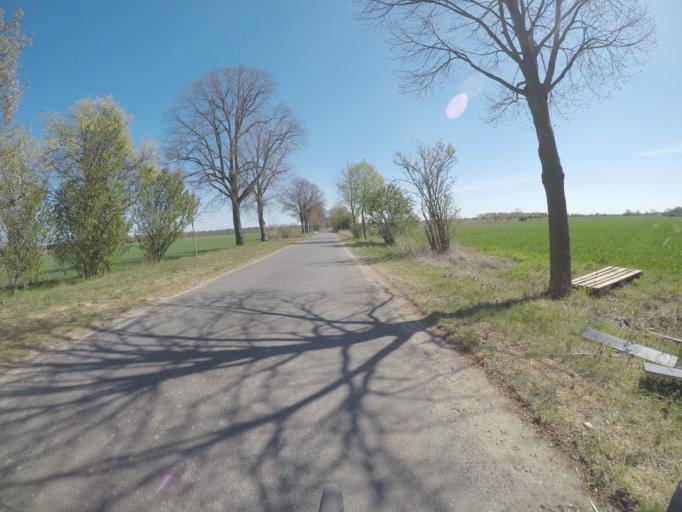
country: DE
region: Brandenburg
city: Falkensee
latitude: 52.5225
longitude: 13.1050
